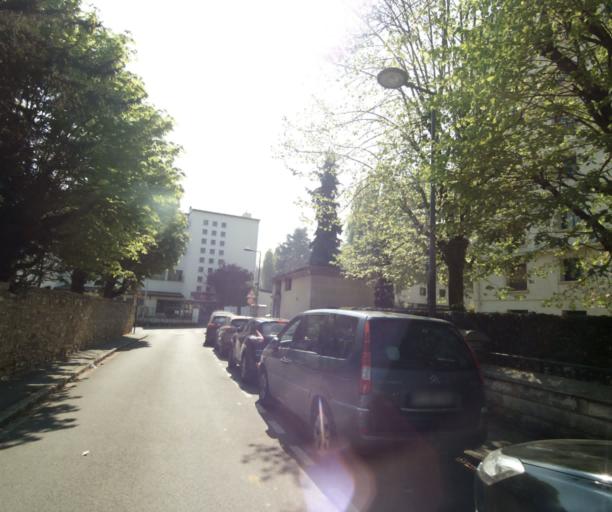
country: FR
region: Ile-de-France
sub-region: Departement des Hauts-de-Seine
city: Sevres
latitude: 48.8186
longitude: 2.2252
